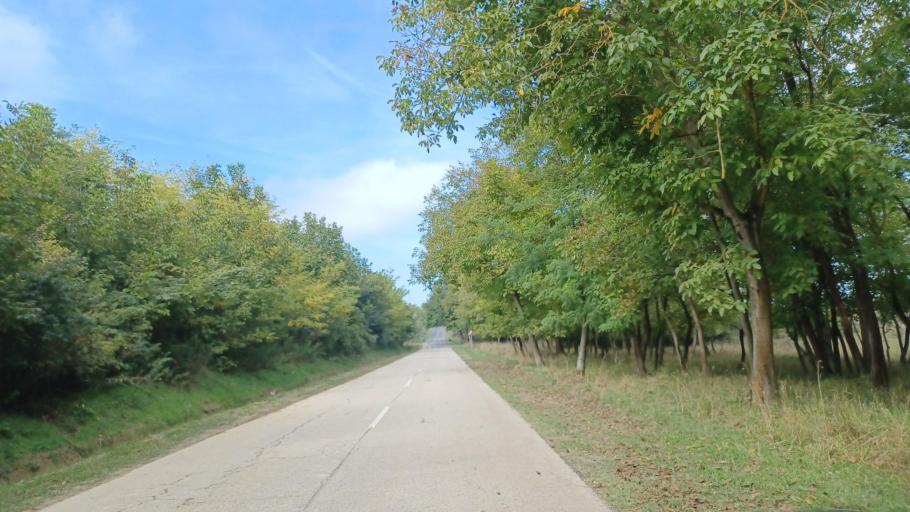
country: HU
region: Tolna
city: Pincehely
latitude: 46.6525
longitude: 18.5117
